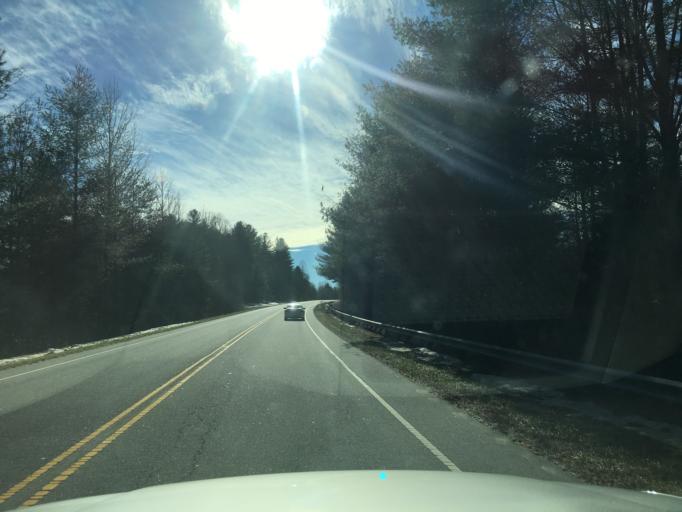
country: US
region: North Carolina
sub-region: Transylvania County
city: Brevard
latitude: 35.1777
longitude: -82.8013
